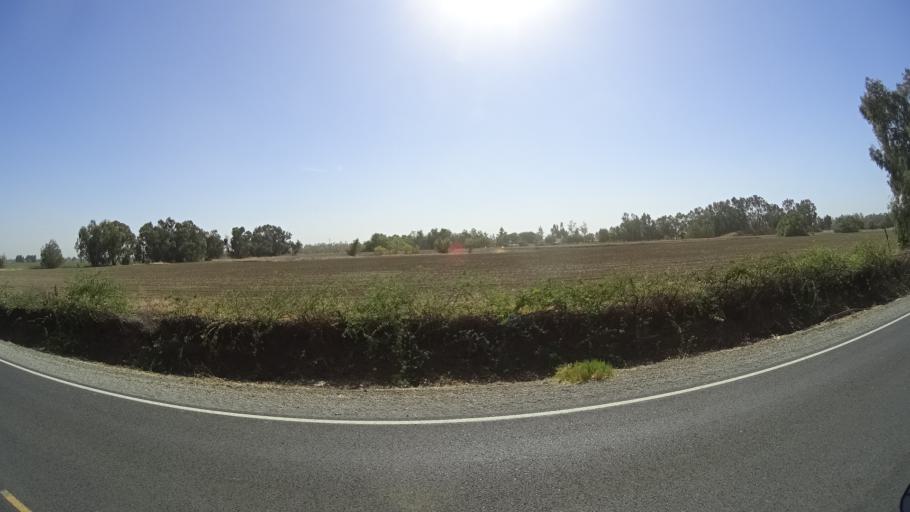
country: US
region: California
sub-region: Yolo County
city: Woodland
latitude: 38.5907
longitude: -121.8508
